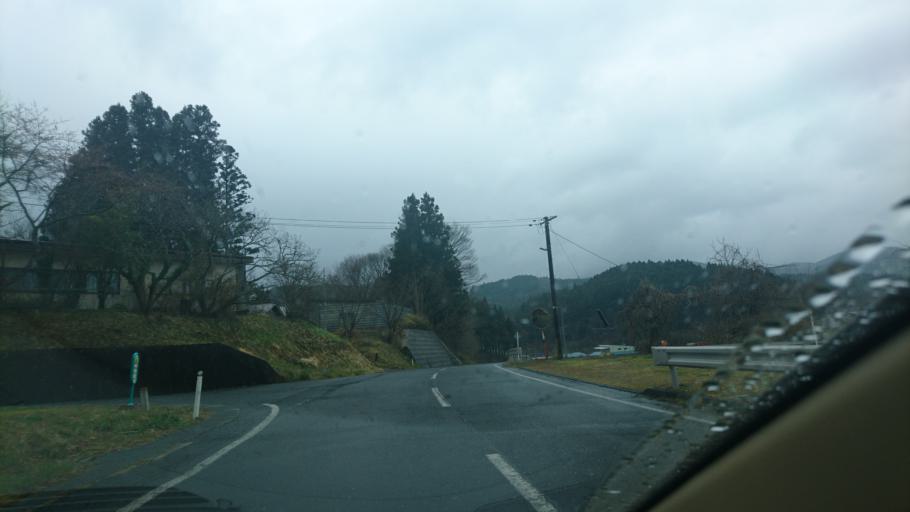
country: JP
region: Iwate
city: Ofunato
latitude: 38.9412
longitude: 141.4614
